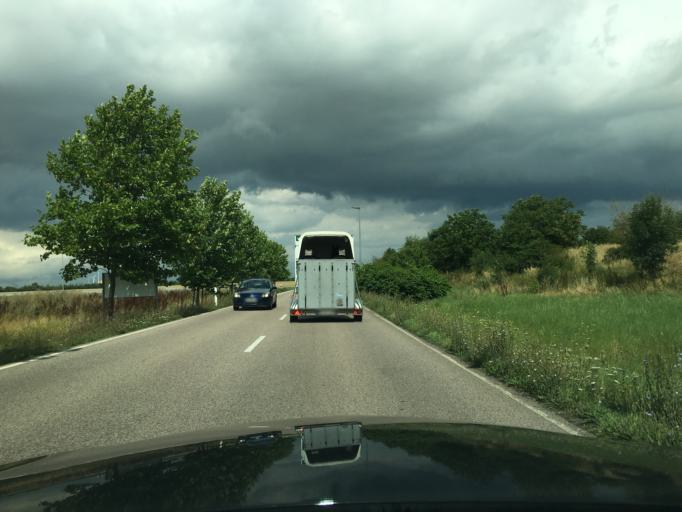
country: DE
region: Saxony-Anhalt
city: Brehna
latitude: 51.5554
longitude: 12.1962
